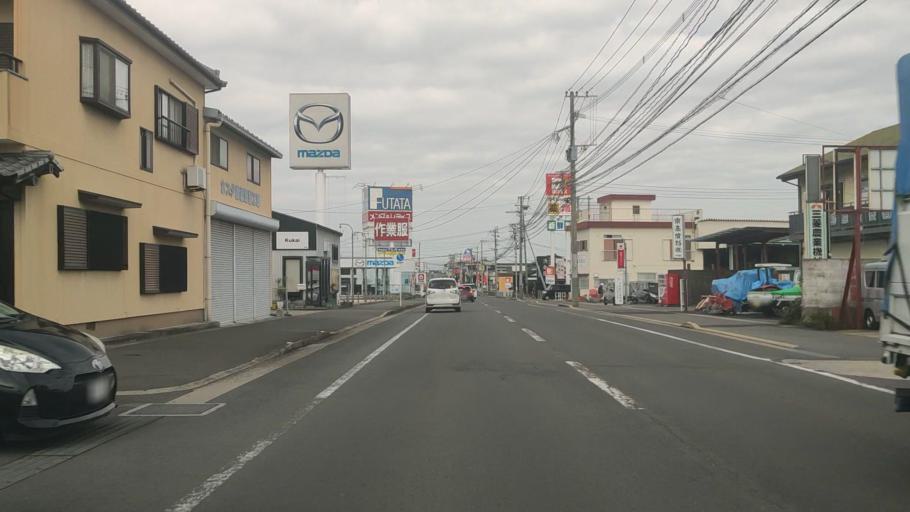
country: JP
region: Nagasaki
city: Shimabara
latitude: 32.8017
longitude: 130.3640
